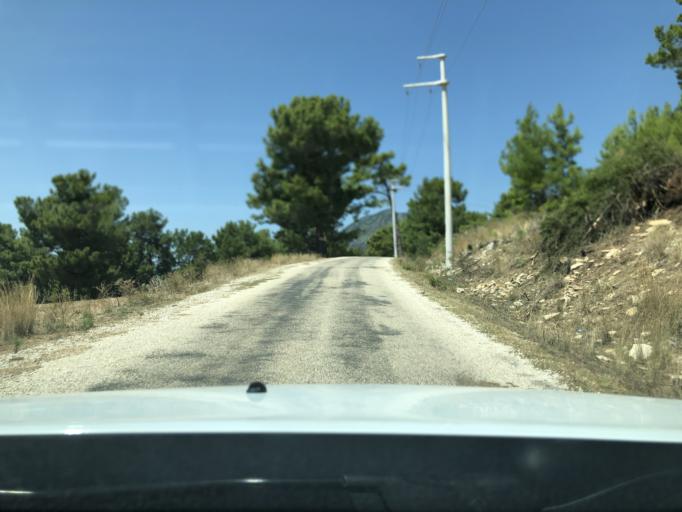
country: TR
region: Antalya
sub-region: Manavgat
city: Manavgat
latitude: 36.8797
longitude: 31.5508
